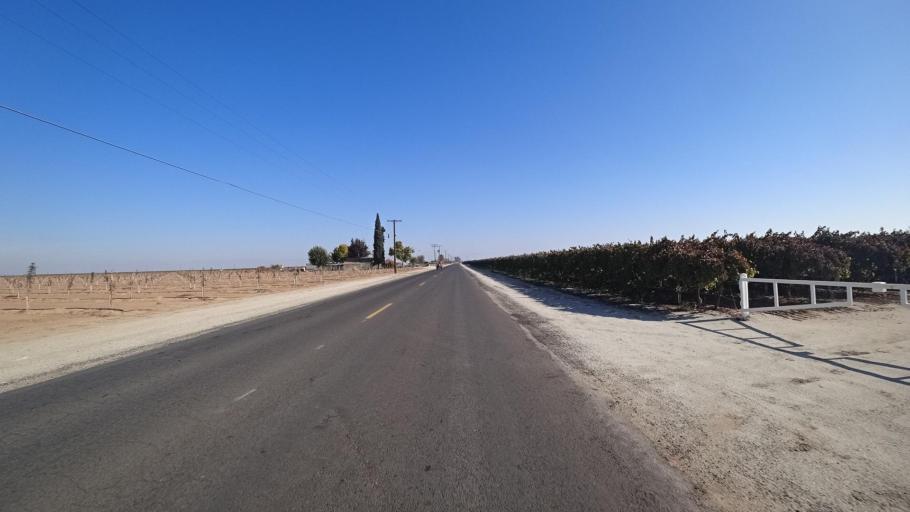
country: US
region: California
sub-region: Kern County
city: McFarland
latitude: 35.6889
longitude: -119.2117
